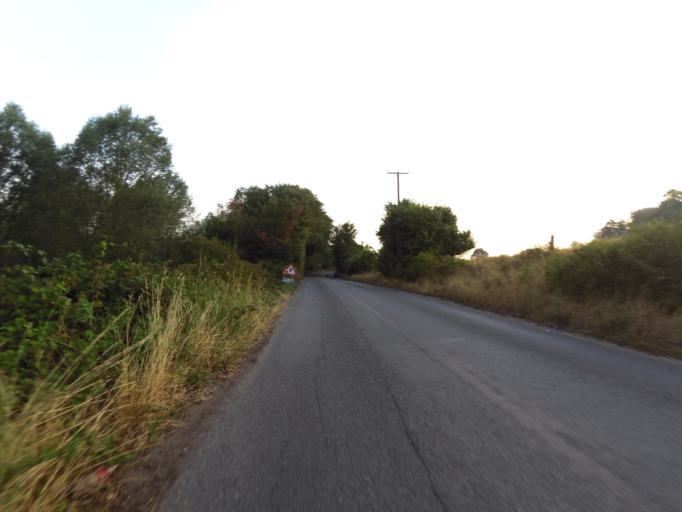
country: GB
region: England
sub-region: Suffolk
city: Bramford
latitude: 52.0946
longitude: 1.1035
